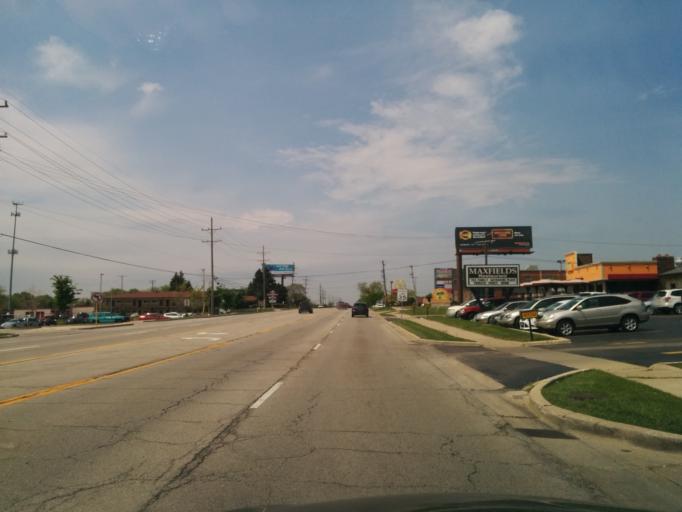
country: US
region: Illinois
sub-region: DuPage County
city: Lombard
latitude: 41.8604
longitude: -88.0075
